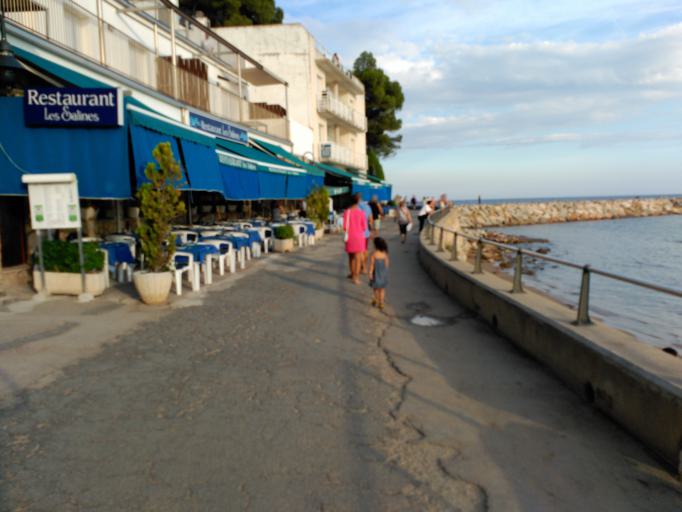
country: ES
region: Catalonia
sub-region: Provincia de Girona
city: Torroella de Montgri
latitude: 42.0537
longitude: 3.2076
